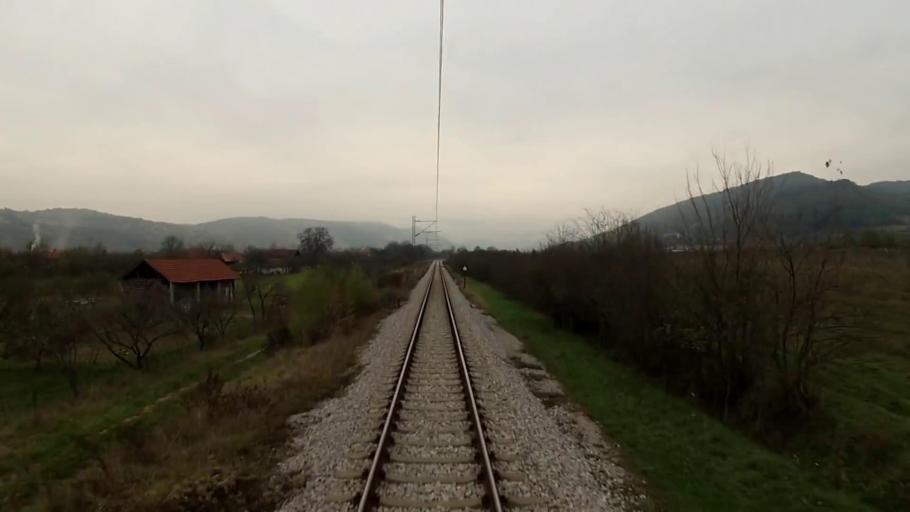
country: RS
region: Central Serbia
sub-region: Pirotski Okrug
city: Dimitrovgrad
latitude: 43.0040
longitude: 22.8142
